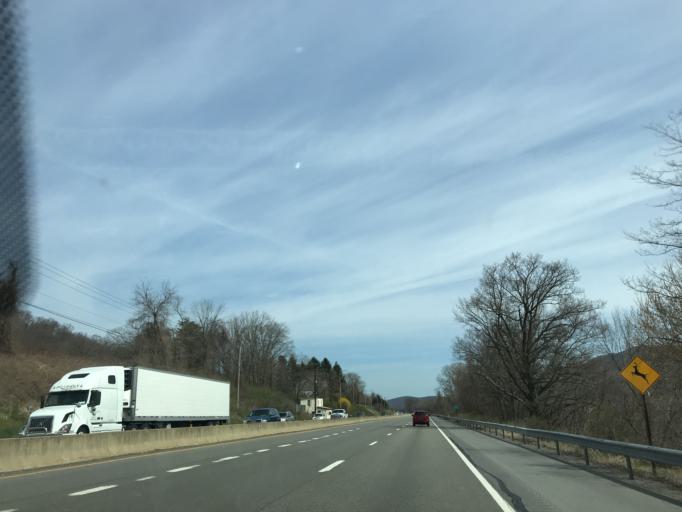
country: US
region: Pennsylvania
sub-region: Snyder County
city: Selinsgrove
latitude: 40.7159
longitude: -76.8594
